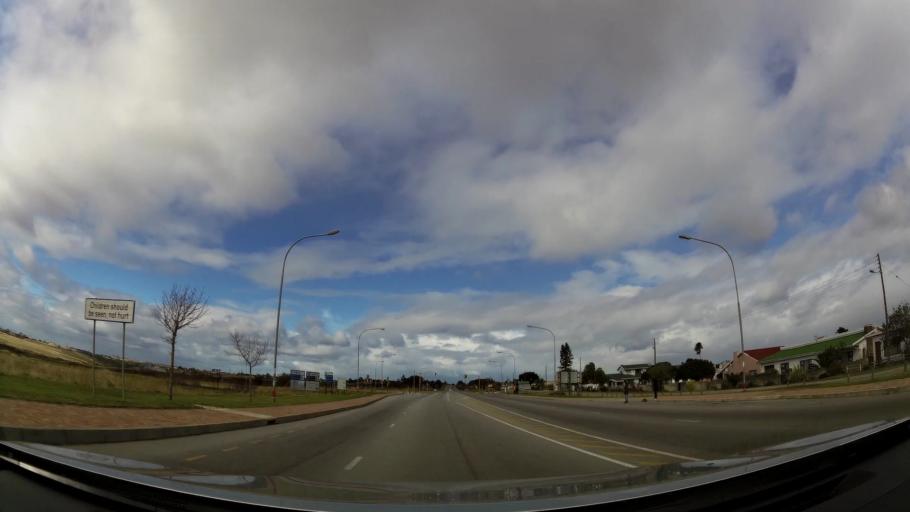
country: ZA
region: Western Cape
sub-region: Eden District Municipality
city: George
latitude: -34.0015
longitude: 22.4466
